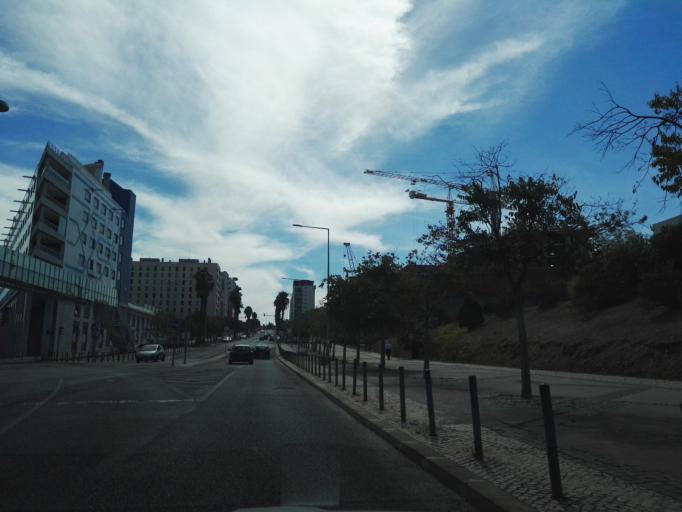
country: PT
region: Lisbon
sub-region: Loures
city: Moscavide
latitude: 38.7593
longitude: -9.0966
